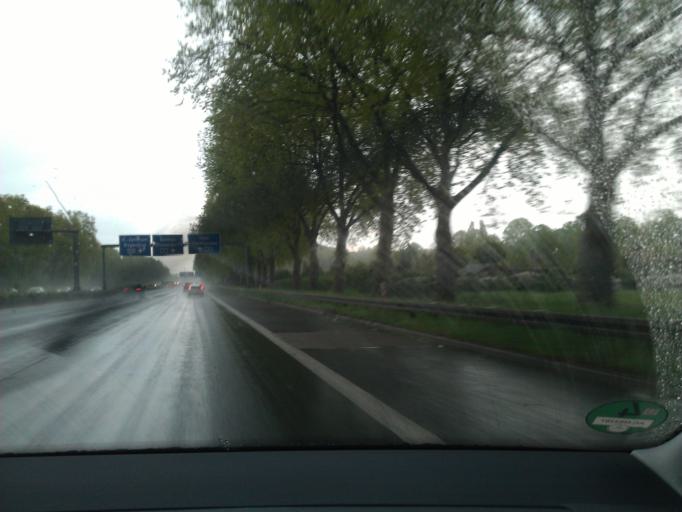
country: DE
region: North Rhine-Westphalia
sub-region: Regierungsbezirk Koln
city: Bayenthal
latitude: 50.8734
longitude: 6.9698
